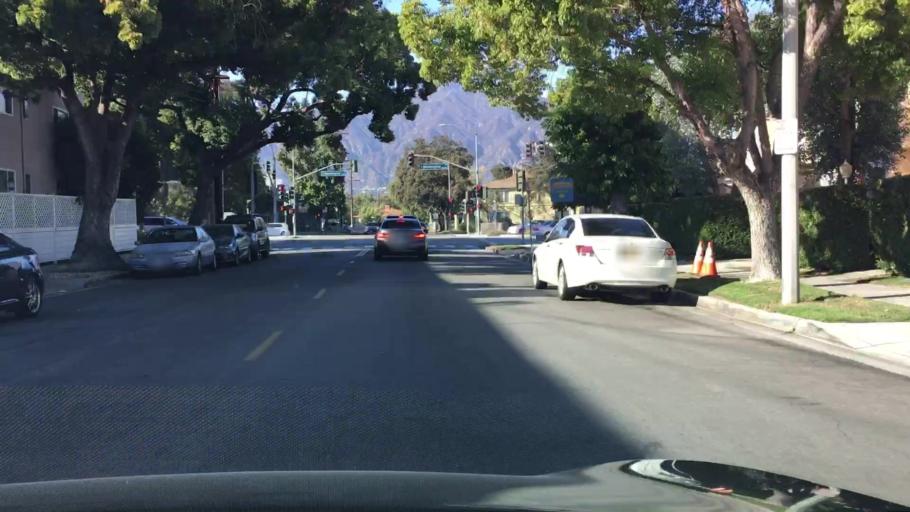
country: US
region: California
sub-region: Los Angeles County
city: Temple City
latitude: 34.1305
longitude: -118.0608
